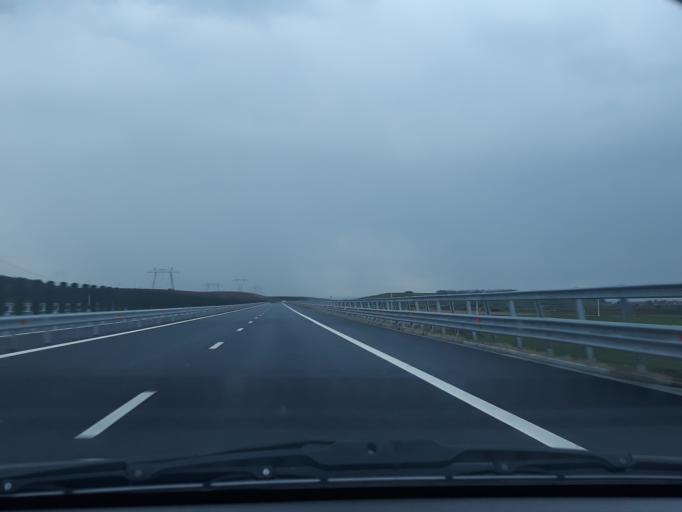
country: RO
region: Mures
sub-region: Comuna Sanpaul
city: Sanpaul
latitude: 46.4430
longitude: 24.3513
